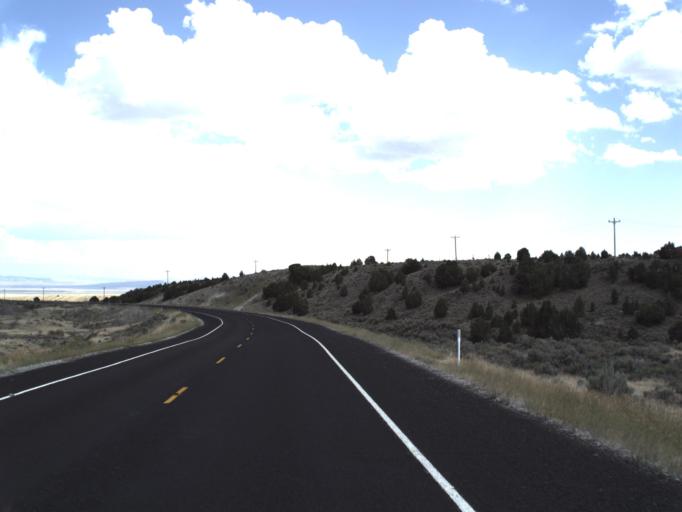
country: US
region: Idaho
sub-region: Minidoka County
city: Rupert
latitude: 41.9759
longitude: -113.1599
